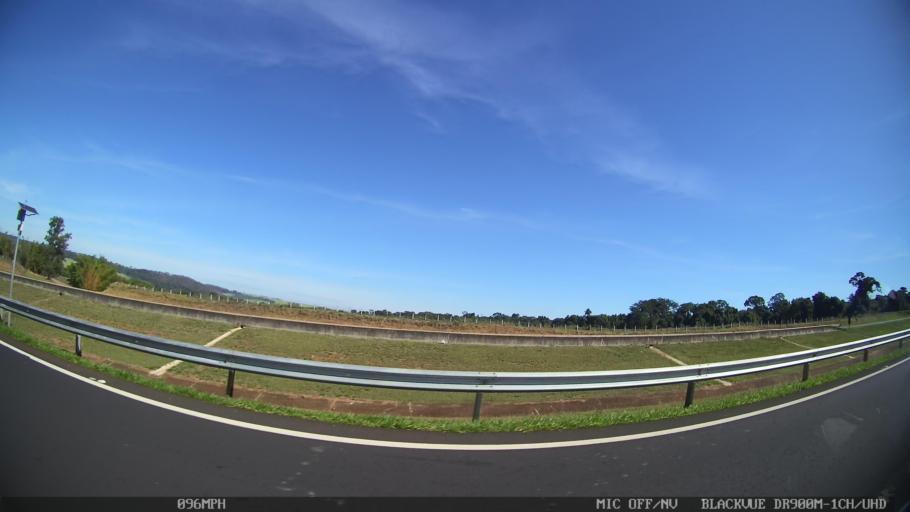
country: BR
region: Sao Paulo
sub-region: Santa Rita Do Passa Quatro
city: Santa Rita do Passa Quatro
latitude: -21.7287
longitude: -47.5856
